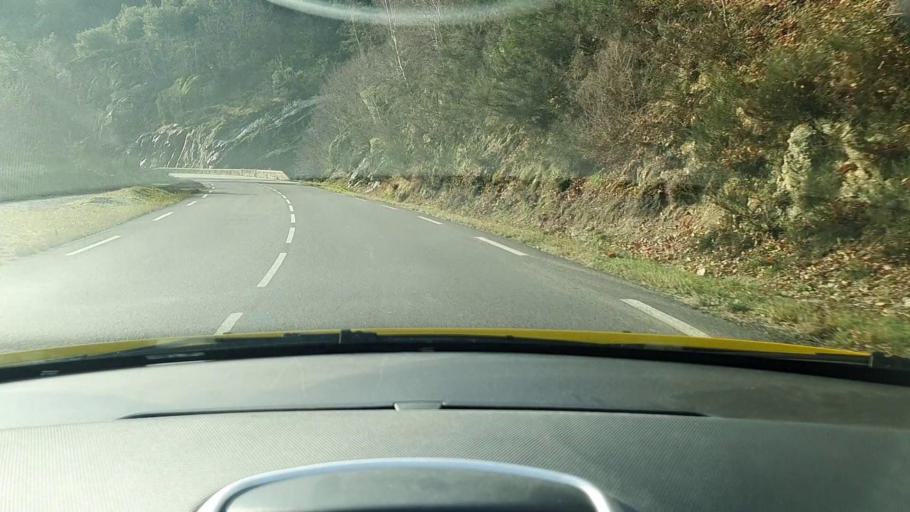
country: FR
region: Languedoc-Roussillon
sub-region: Departement du Gard
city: Branoux-les-Taillades
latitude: 44.4038
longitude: 3.9323
